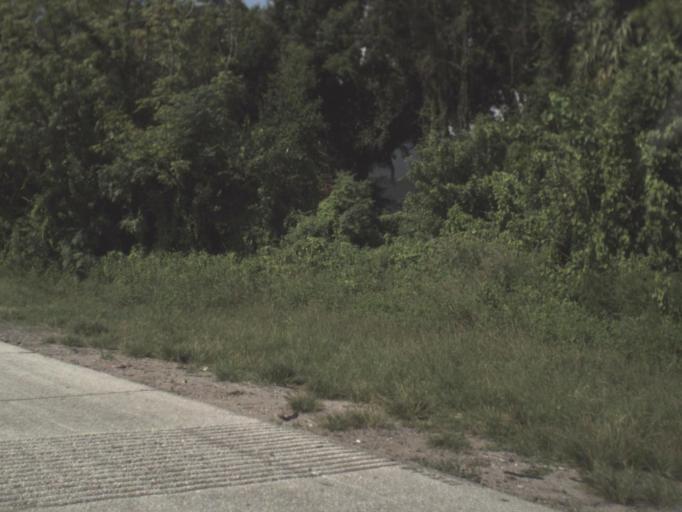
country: US
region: Florida
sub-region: Hillsborough County
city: Mango
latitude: 27.9635
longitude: -82.3266
